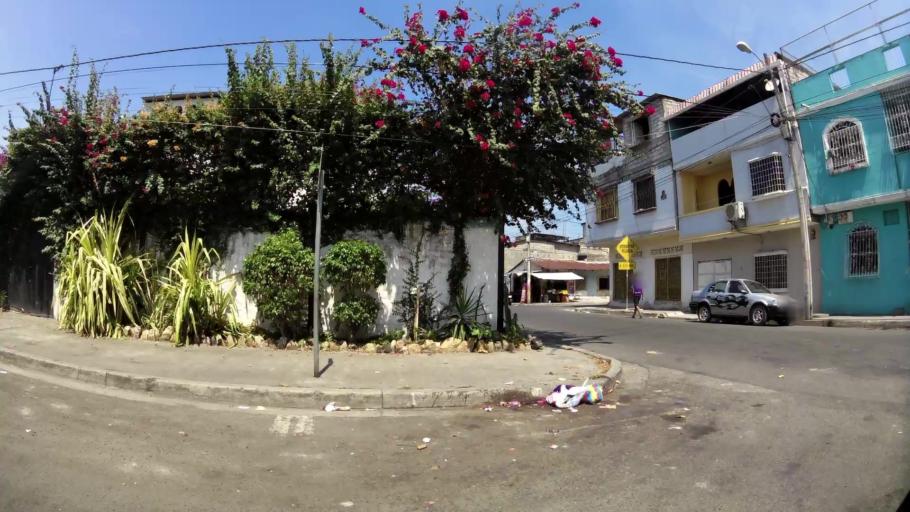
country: EC
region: Guayas
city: Guayaquil
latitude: -2.2372
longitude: -79.9057
